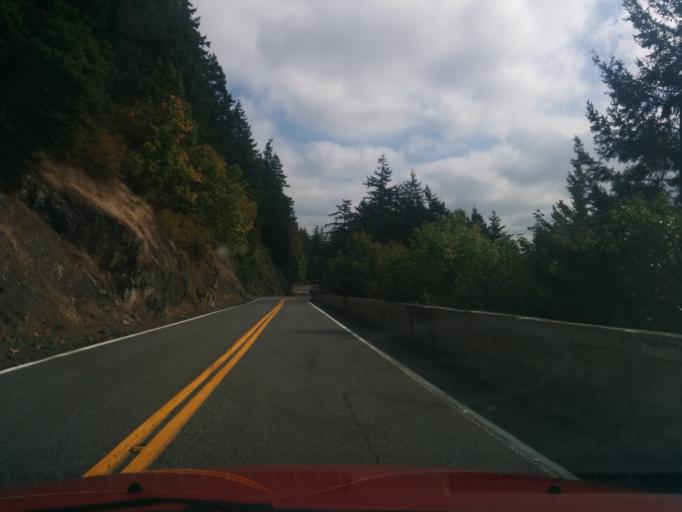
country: US
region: Washington
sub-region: Whatcom County
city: Bellingham
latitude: 48.6296
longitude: -122.4672
